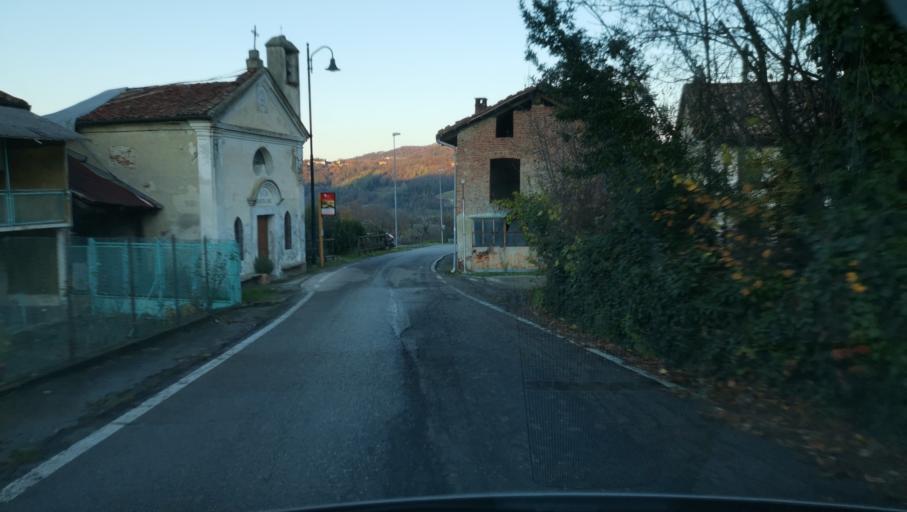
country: IT
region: Piedmont
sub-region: Provincia di Asti
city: Moncucco Torinese
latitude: 45.0638
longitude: 7.9374
